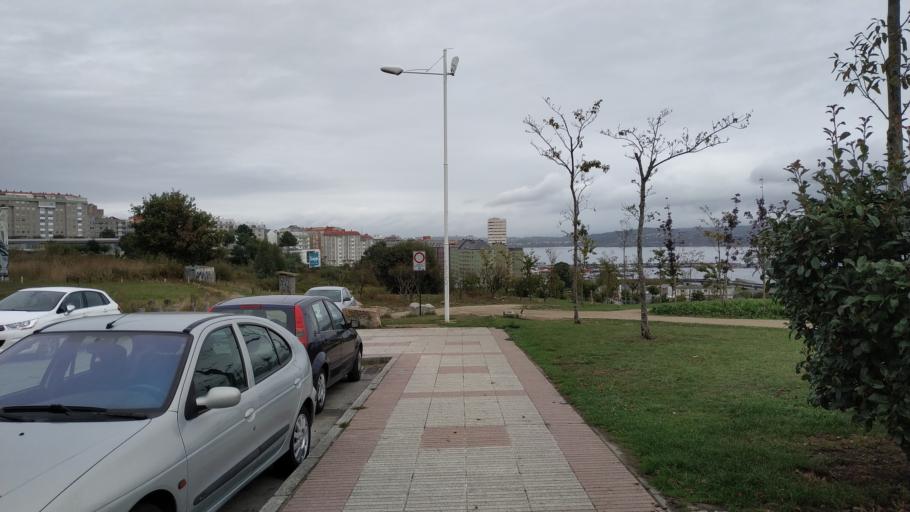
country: ES
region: Galicia
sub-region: Provincia da Coruna
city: A Coruna
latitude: 43.3477
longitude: -8.3950
